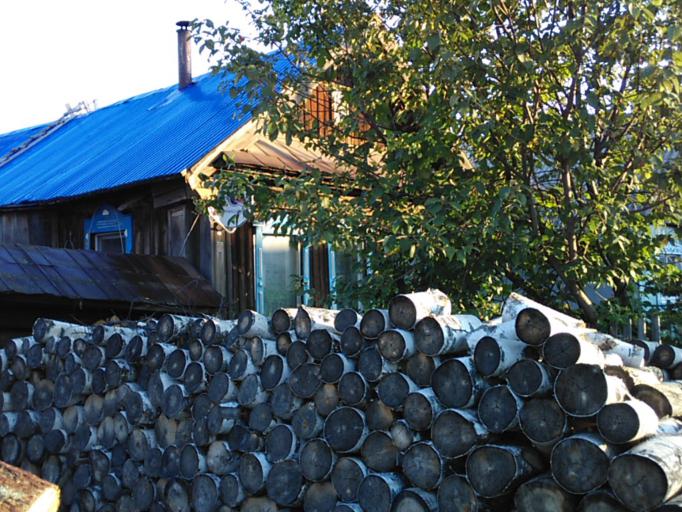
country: RU
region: Perm
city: Foki
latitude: 56.6934
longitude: 54.3493
